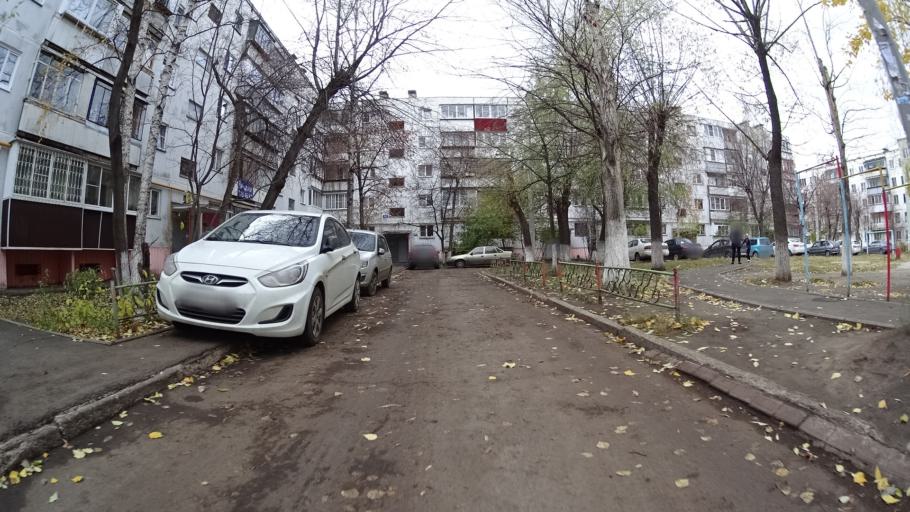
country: RU
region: Chelyabinsk
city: Roshchino
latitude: 55.1927
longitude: 61.3092
